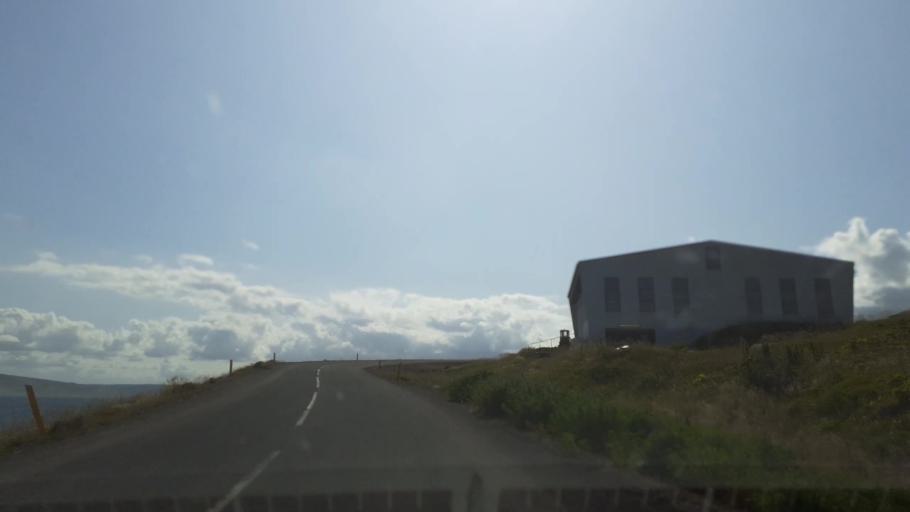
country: IS
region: West
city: Borgarnes
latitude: 65.2079
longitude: -21.0972
